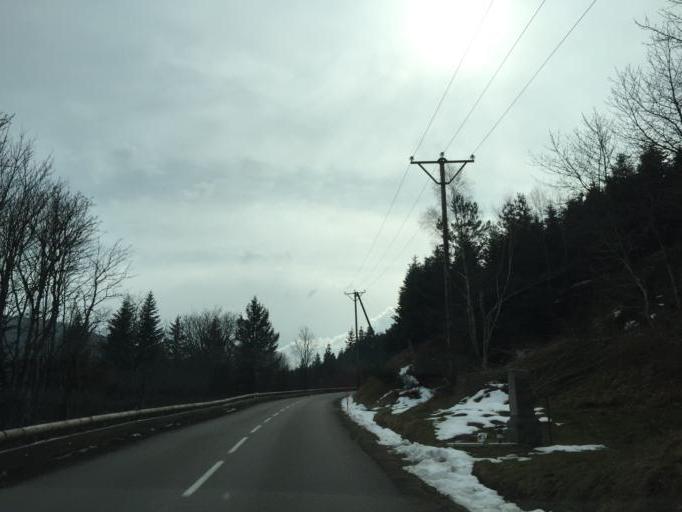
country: FR
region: Rhone-Alpes
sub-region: Departement de la Loire
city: Saint-Chamond
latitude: 45.3869
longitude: 4.5306
